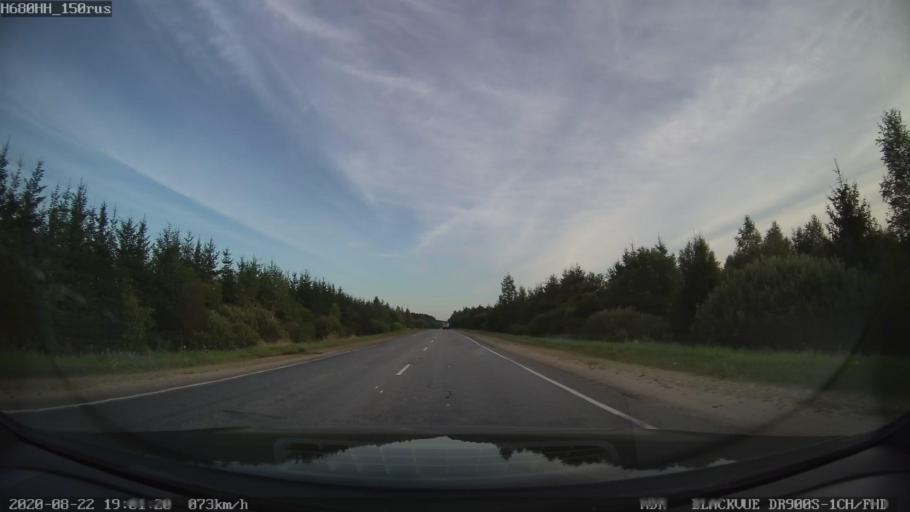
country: RU
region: Tverskaya
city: Vasil'yevskiy Mokh
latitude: 57.1203
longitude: 36.1143
